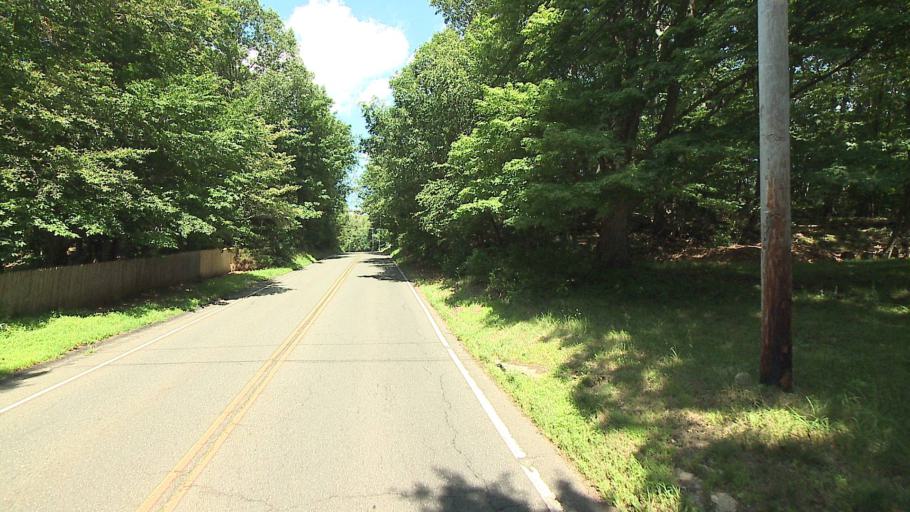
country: US
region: Connecticut
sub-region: Fairfield County
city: Shelton
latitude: 41.3020
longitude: -73.1324
